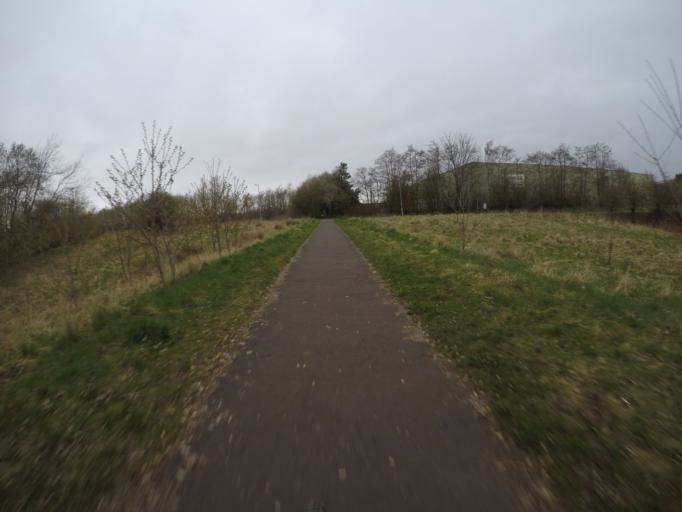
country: GB
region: Scotland
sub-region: North Ayrshire
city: Irvine
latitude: 55.6139
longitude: -4.6420
